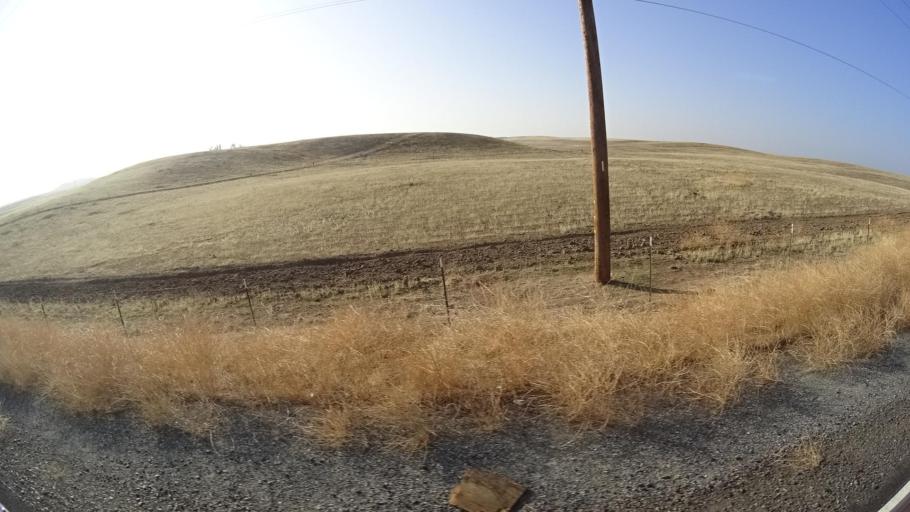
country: US
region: California
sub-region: Tulare County
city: Richgrove
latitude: 35.7620
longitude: -119.0374
